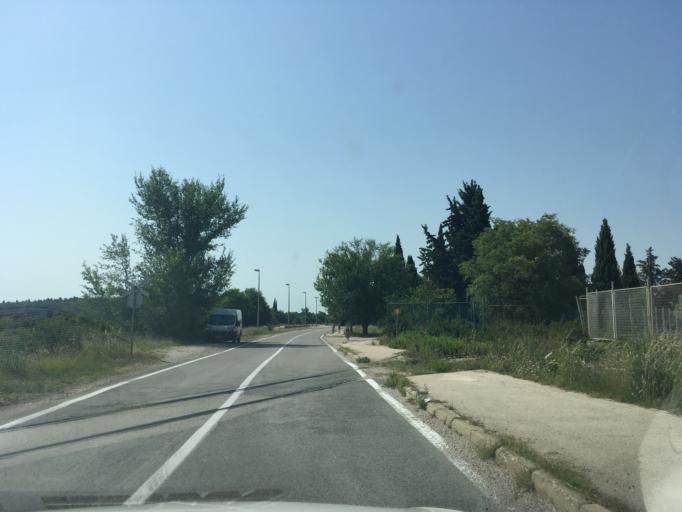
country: HR
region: Zadarska
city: Benkovac
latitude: 44.0250
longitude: 15.6173
